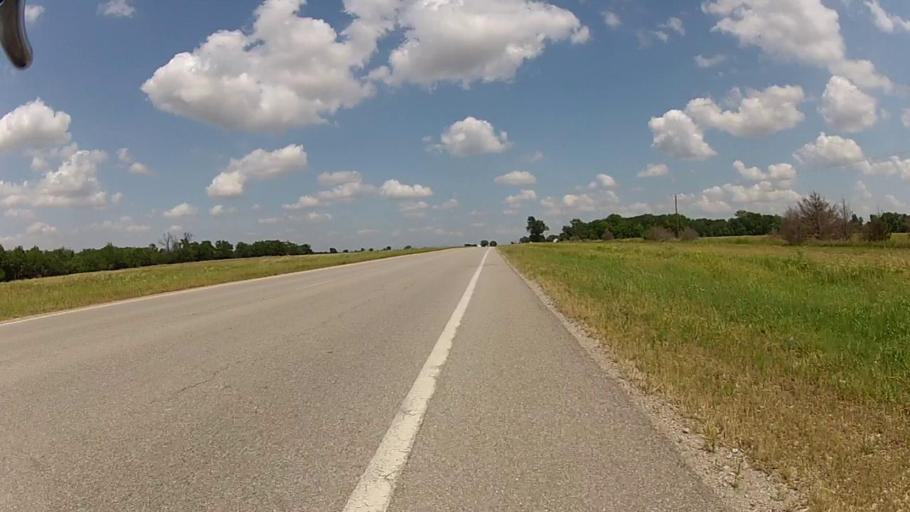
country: US
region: Kansas
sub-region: Labette County
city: Oswego
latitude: 37.1938
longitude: -95.1855
